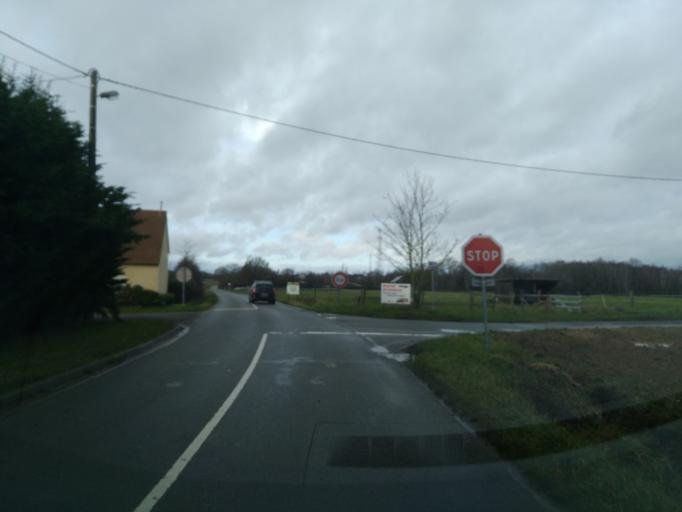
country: FR
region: Ile-de-France
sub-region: Departement des Yvelines
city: Les Alluets-le-Roi
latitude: 48.9022
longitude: 1.9418
